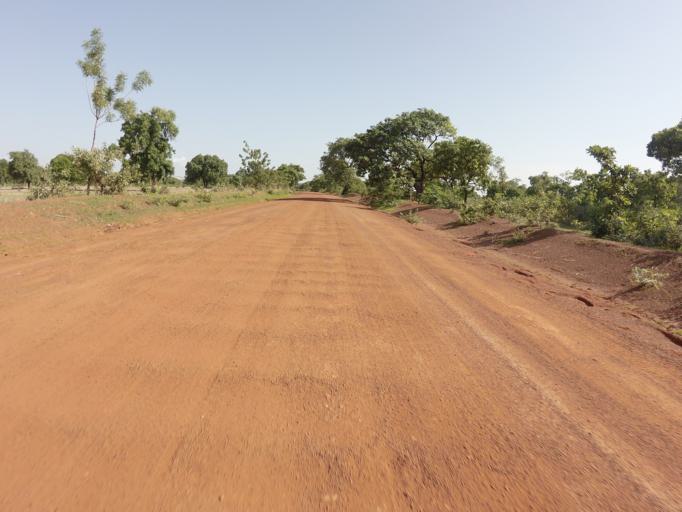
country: GH
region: Upper East
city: Bawku
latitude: 10.7506
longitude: -0.1999
